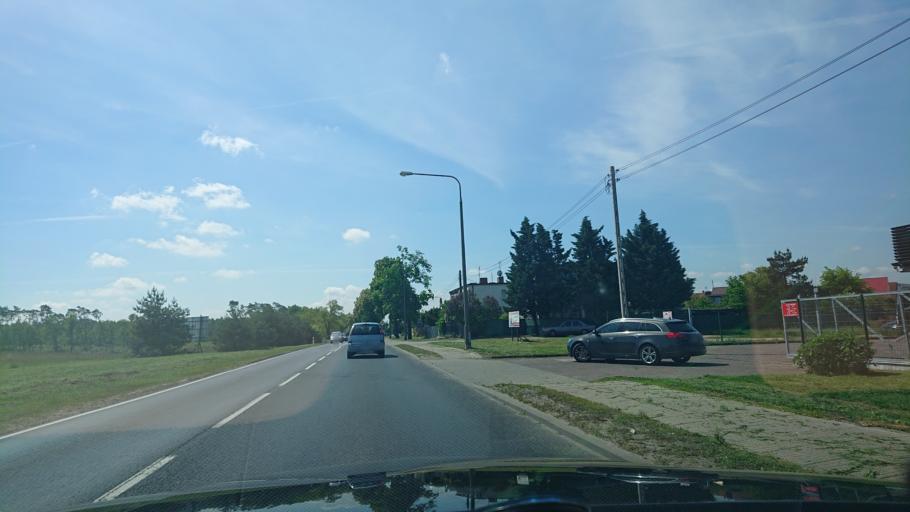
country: PL
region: Greater Poland Voivodeship
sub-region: Powiat gnieznienski
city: Gniezno
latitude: 52.5089
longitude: 17.5949
